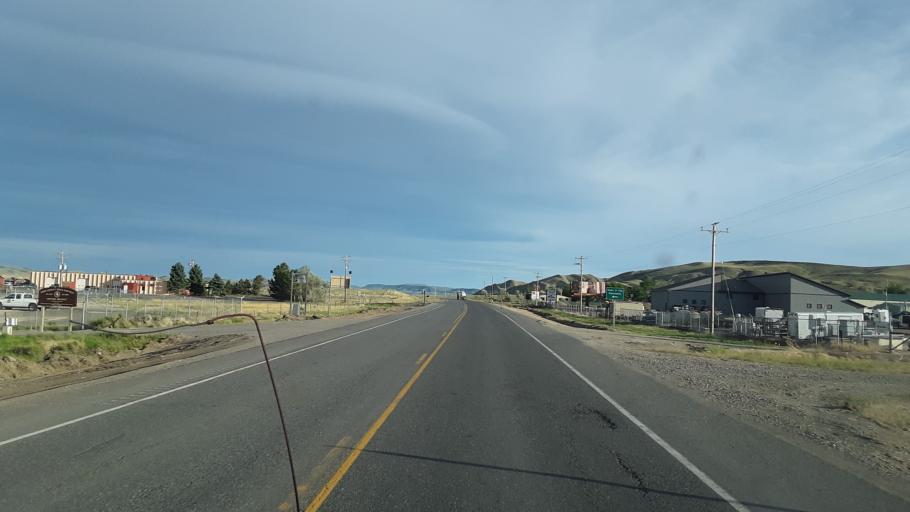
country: US
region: Wyoming
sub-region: Park County
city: Cody
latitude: 44.4975
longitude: -109.0253
